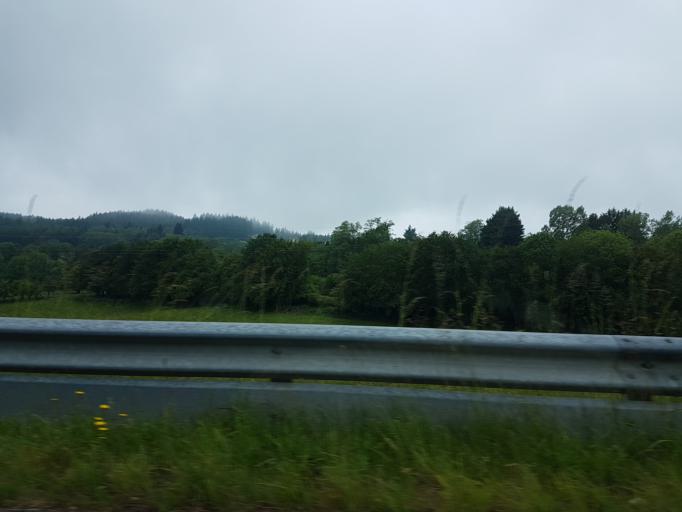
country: FR
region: Bourgogne
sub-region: Departement de la Nievre
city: Chateau-Chinon(Ville)
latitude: 47.0545
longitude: 3.9348
